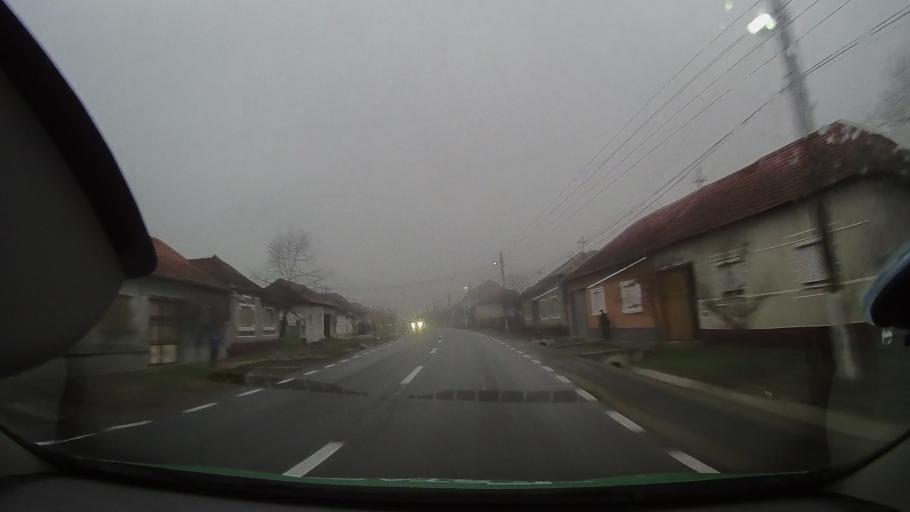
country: RO
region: Bihor
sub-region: Comuna Olcea
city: Calacea
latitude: 46.6362
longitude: 21.9561
